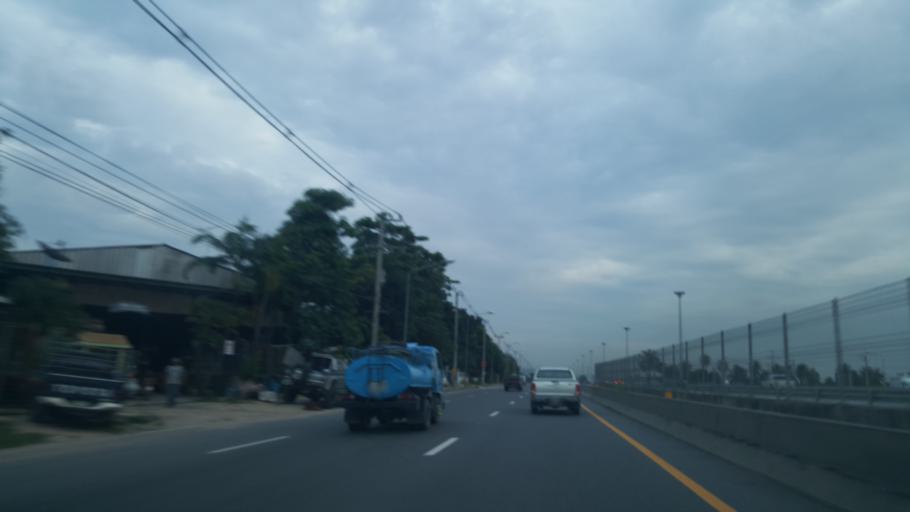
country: TH
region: Chon Buri
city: Ban Talat Bueng
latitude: 13.0834
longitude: 100.9924
